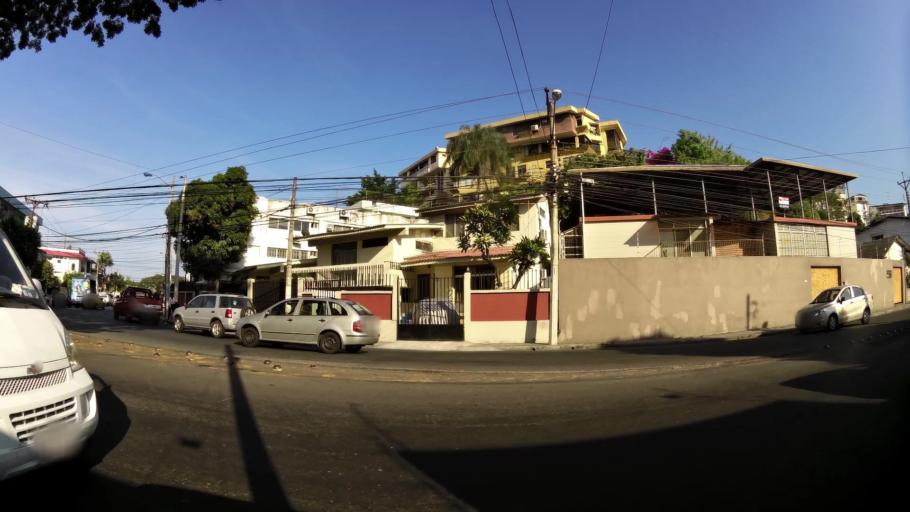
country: EC
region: Guayas
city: Guayaquil
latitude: -2.1664
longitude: -79.9018
